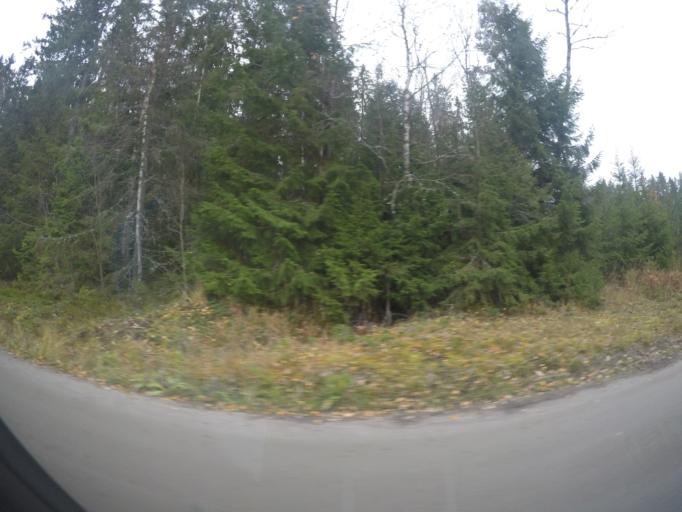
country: SE
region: Vaestmanland
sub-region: Surahammars Kommun
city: Ramnas
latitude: 59.7230
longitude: 16.0933
